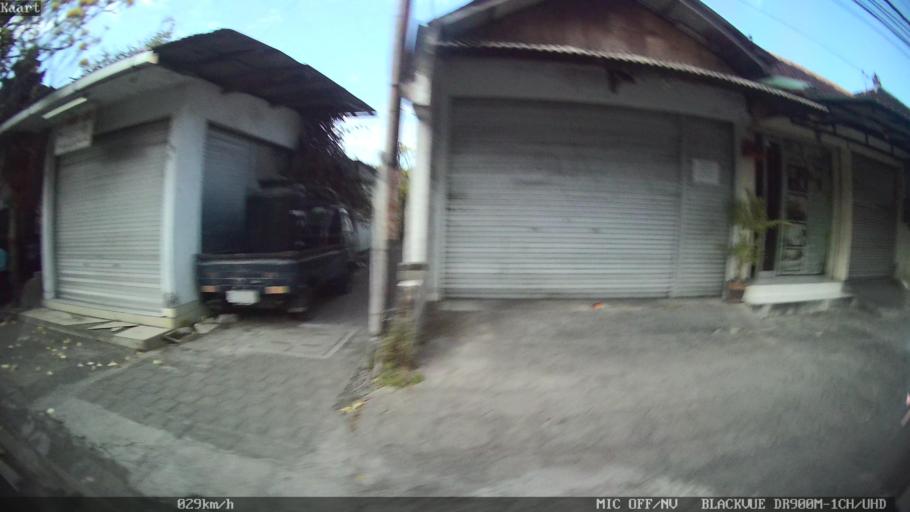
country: ID
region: Bali
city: Karyadharma
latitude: -8.6850
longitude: 115.2076
